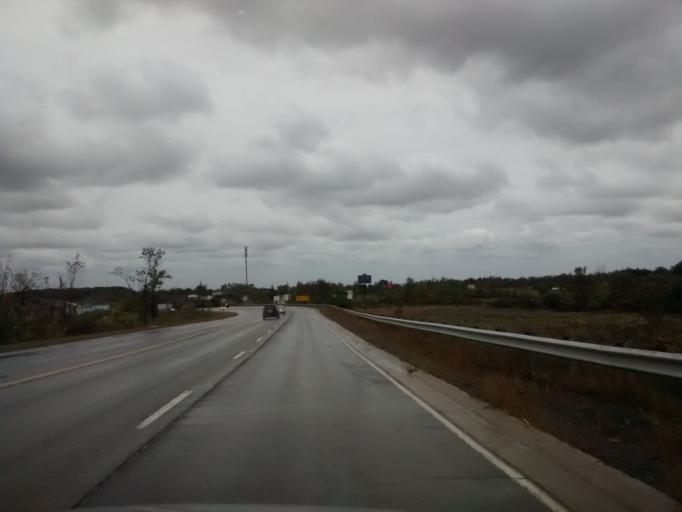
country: CA
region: Ontario
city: Hamilton
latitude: 43.2009
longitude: -79.7645
